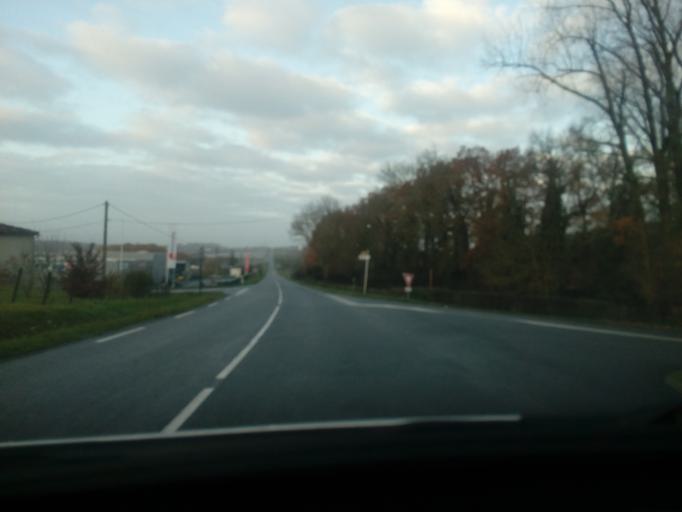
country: FR
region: Poitou-Charentes
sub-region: Departement de la Charente-Maritime
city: Jonzac
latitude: 45.4457
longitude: -0.3781
